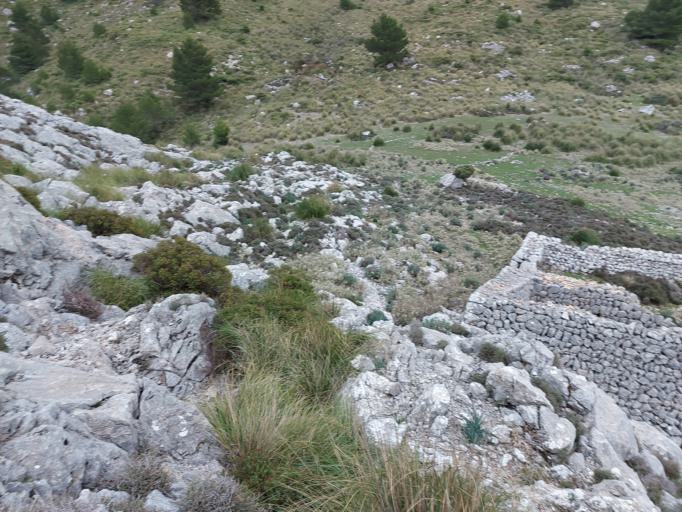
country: ES
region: Balearic Islands
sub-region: Illes Balears
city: Escorca
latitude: 39.8124
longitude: 2.8412
